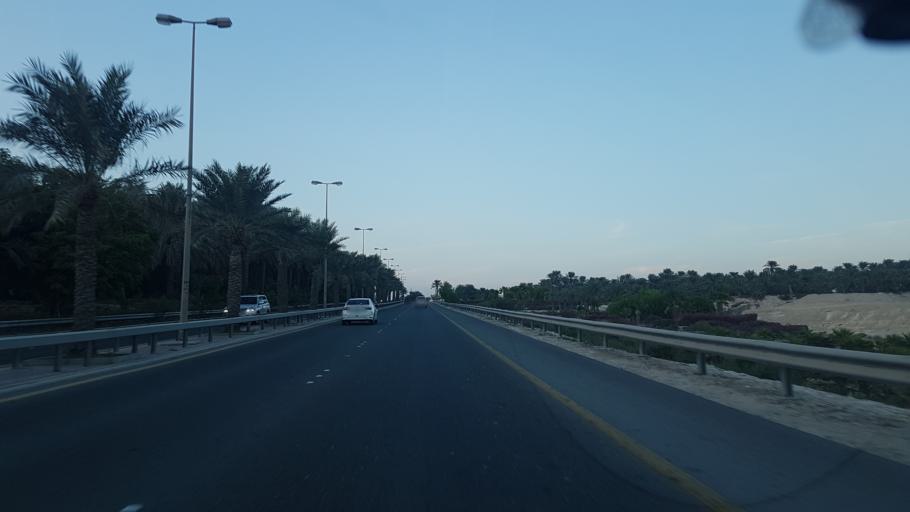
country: BH
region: Northern
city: Ar Rifa'
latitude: 26.1153
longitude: 50.5373
